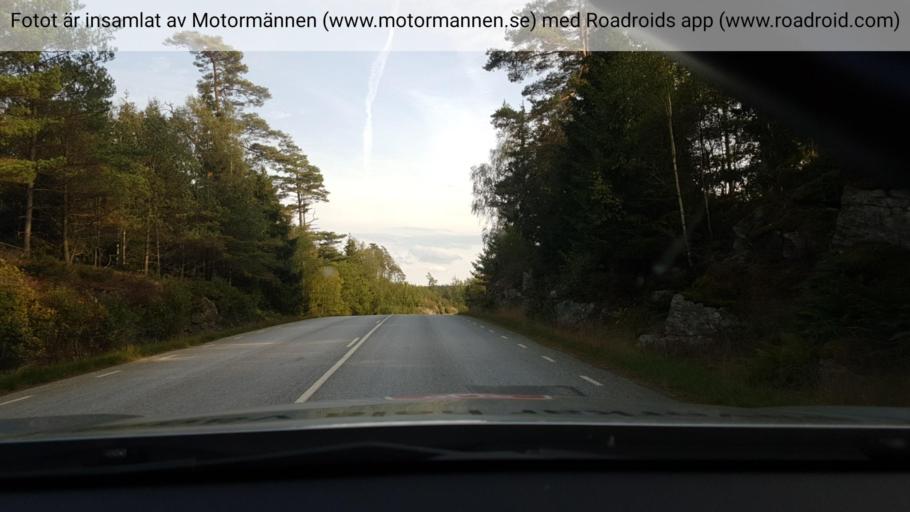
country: SE
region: Vaestra Goetaland
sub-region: Uddevalla Kommun
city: Ljungskile
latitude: 58.1346
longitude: 11.9782
